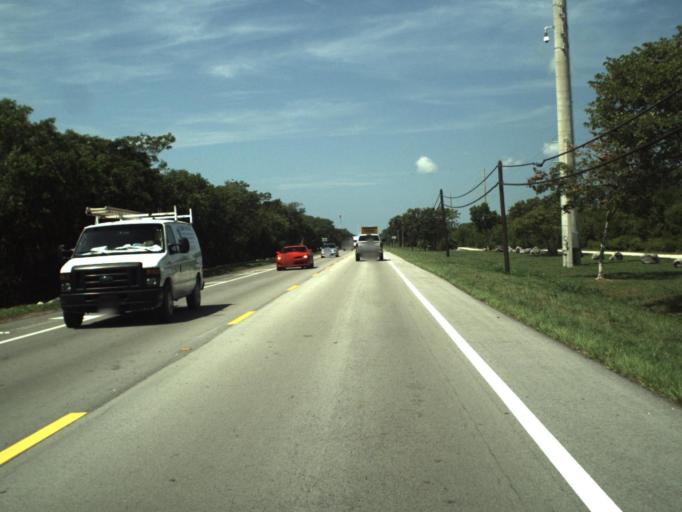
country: US
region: Florida
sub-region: Monroe County
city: Marathon
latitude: 24.7401
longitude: -80.9997
